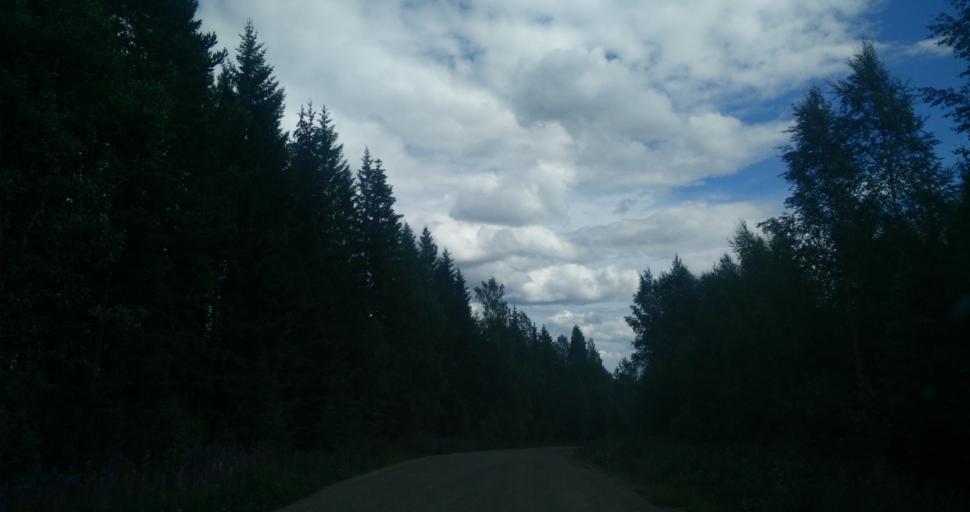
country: SE
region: Gaevleborg
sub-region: Nordanstigs Kommun
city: Bergsjoe
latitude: 62.0738
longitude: 16.7631
